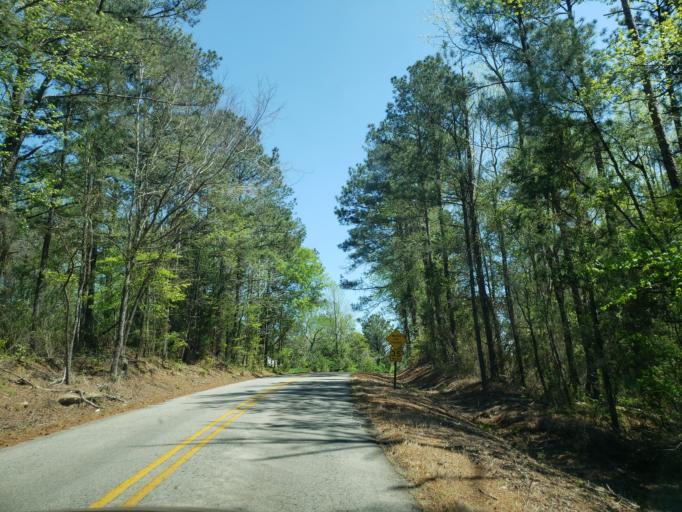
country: US
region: Alabama
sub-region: Tallapoosa County
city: Camp Hill
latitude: 32.6864
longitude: -85.6830
